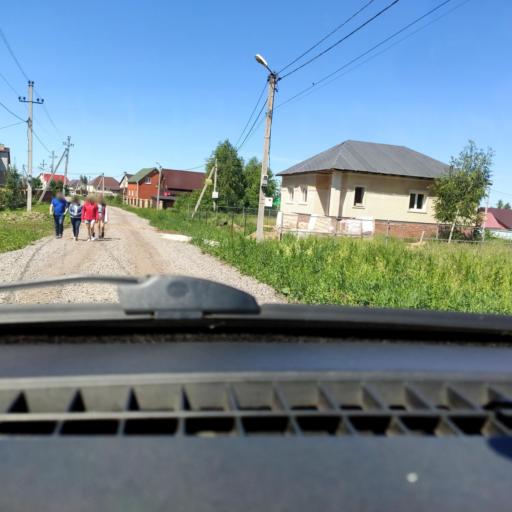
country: RU
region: Bashkortostan
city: Iglino
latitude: 54.7967
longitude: 56.2824
